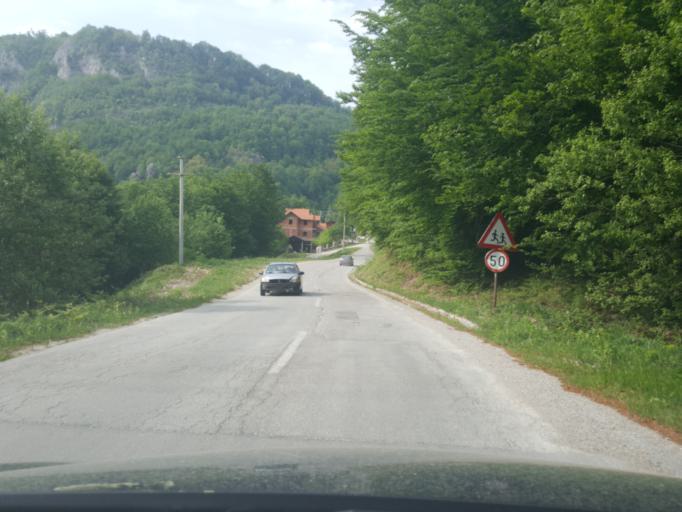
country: RS
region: Central Serbia
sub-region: Zlatiborski Okrug
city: Bajina Basta
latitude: 44.0878
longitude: 19.6598
